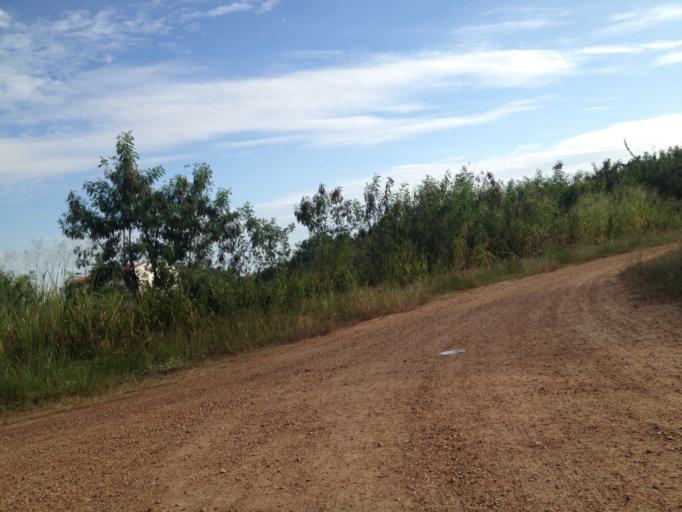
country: TH
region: Chiang Mai
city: Chiang Mai
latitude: 18.7591
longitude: 98.9382
